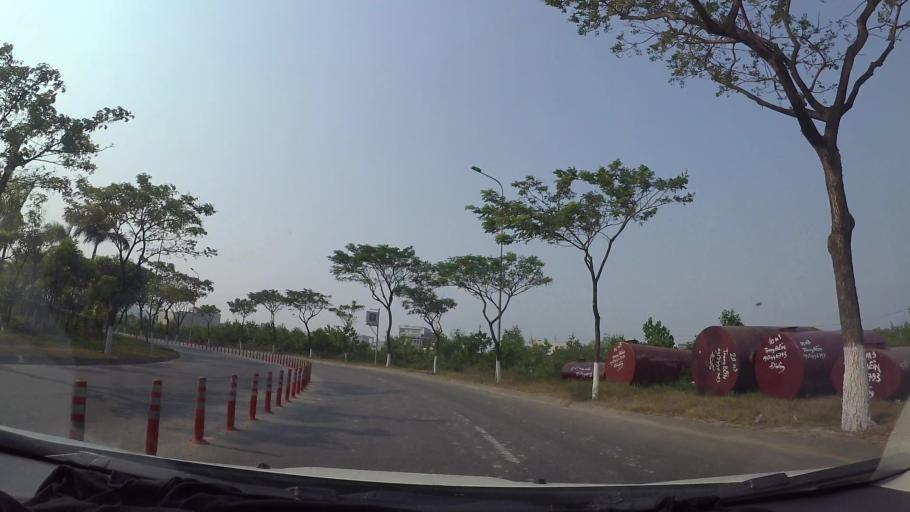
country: VN
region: Da Nang
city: Cam Le
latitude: 16.0147
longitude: 108.1955
